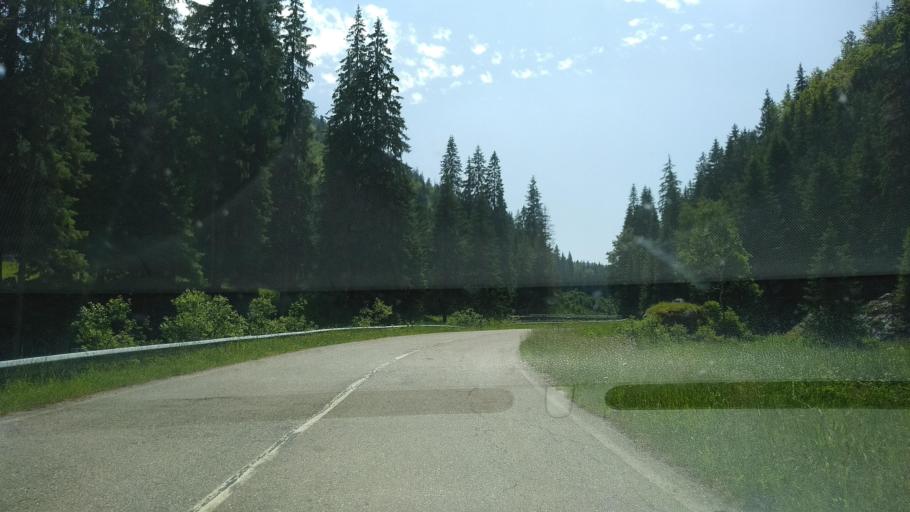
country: RO
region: Gorj
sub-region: Comuna Tismana
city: Sohodol
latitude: 45.2673
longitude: 22.8805
